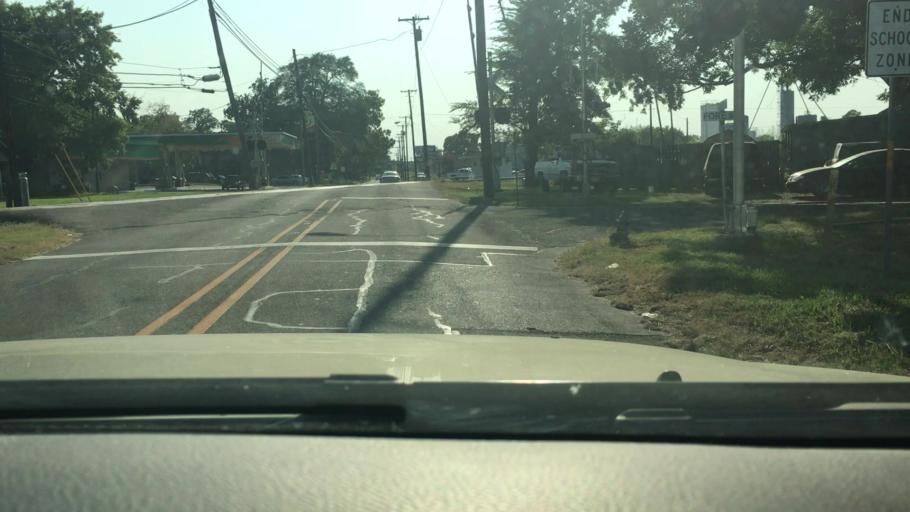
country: US
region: Texas
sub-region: Hopkins County
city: Sulphur Springs
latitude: 33.1353
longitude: -95.6099
